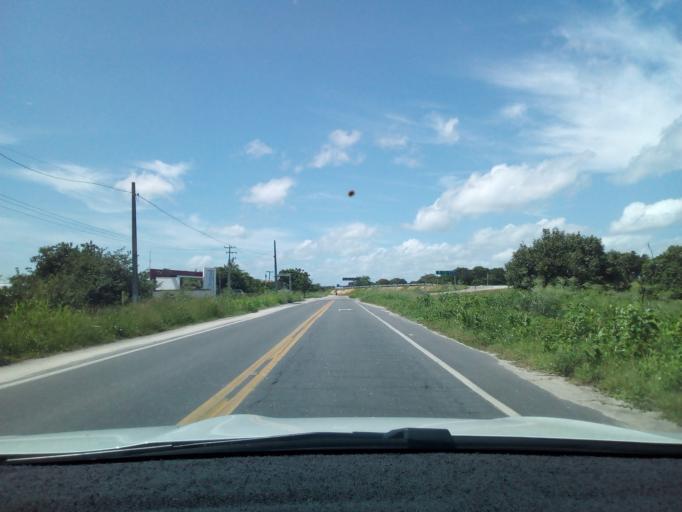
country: BR
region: Ceara
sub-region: Beberibe
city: Beberibe
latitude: -4.1853
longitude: -38.1361
